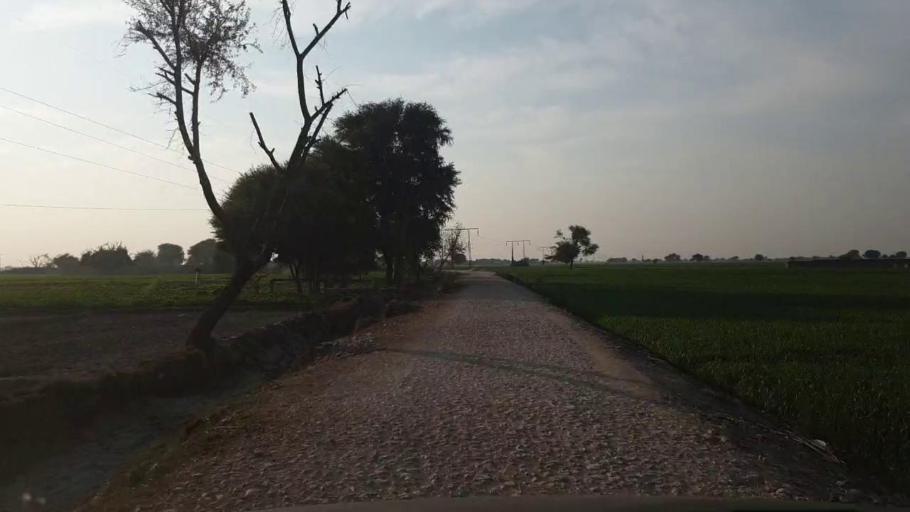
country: PK
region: Sindh
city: Shahpur Chakar
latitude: 26.1526
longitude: 68.6267
